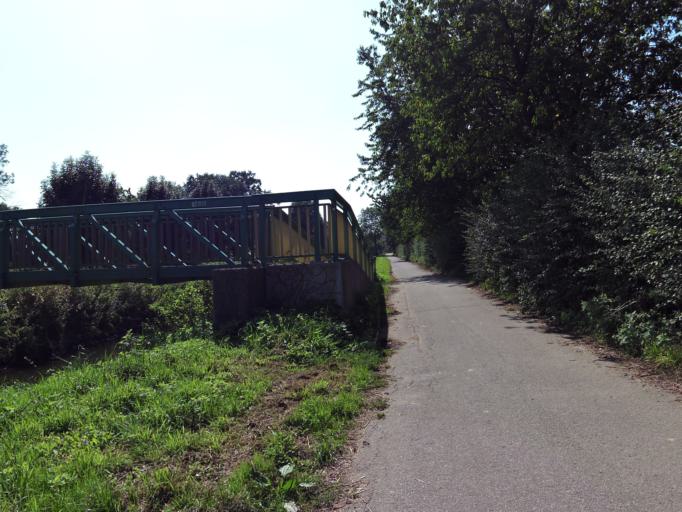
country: DE
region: North Rhine-Westphalia
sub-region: Regierungsbezirk Koln
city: Ubach-Palenberg
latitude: 50.9383
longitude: 6.0992
